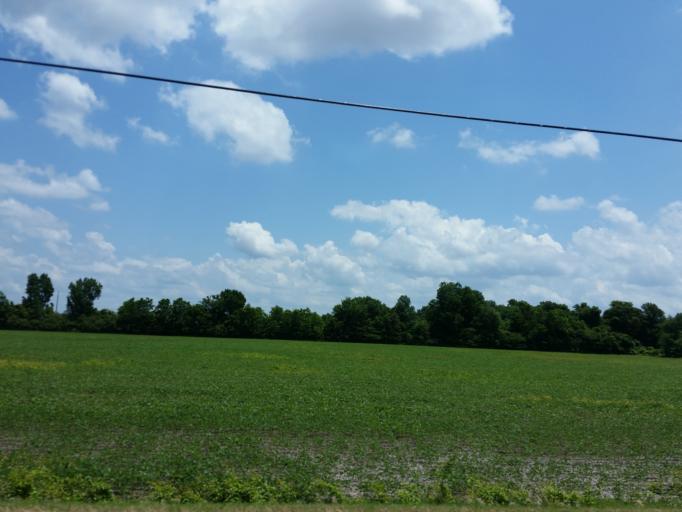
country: US
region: Tennessee
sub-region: Lake County
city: Tiptonville
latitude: 36.3658
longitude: -89.4686
